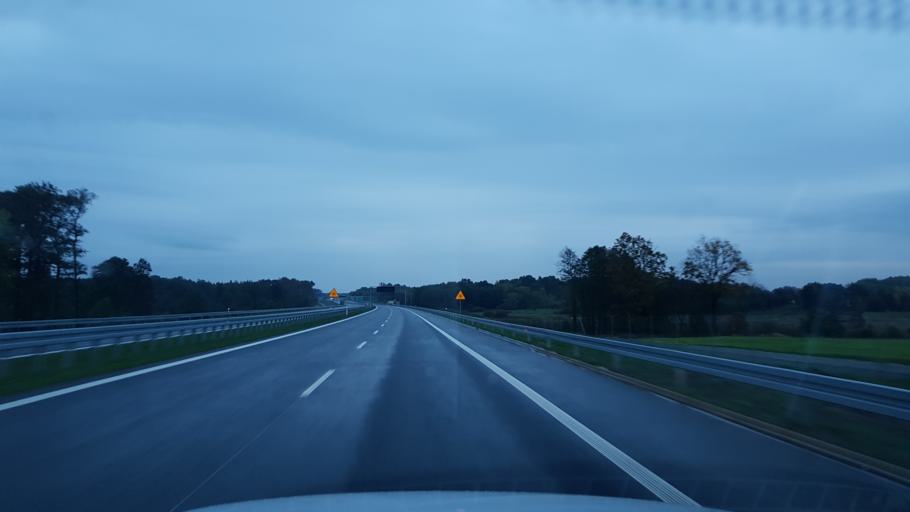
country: PL
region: West Pomeranian Voivodeship
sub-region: Powiat gryficki
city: Brojce
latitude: 53.9273
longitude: 15.3892
